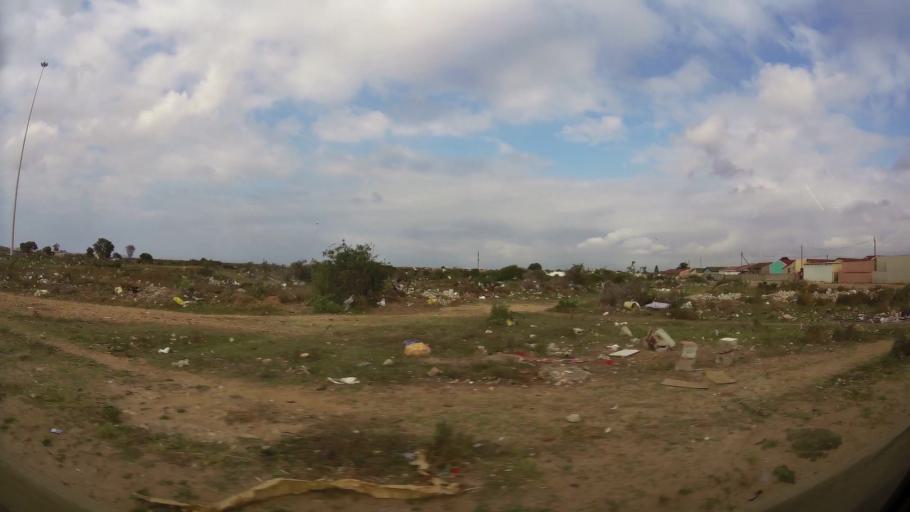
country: ZA
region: Eastern Cape
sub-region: Nelson Mandela Bay Metropolitan Municipality
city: Port Elizabeth
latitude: -33.8139
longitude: 25.5893
